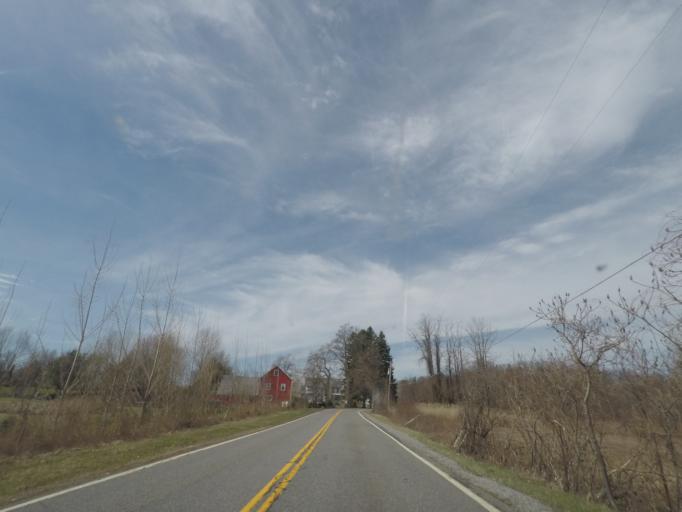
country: US
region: New York
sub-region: Saratoga County
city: Country Knolls
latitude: 42.9032
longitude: -73.7484
